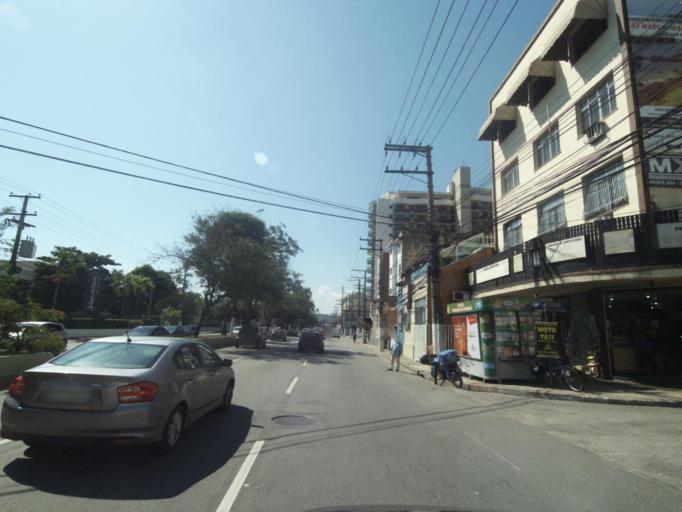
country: BR
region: Rio de Janeiro
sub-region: Niteroi
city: Niteroi
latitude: -22.8917
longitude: -43.1138
